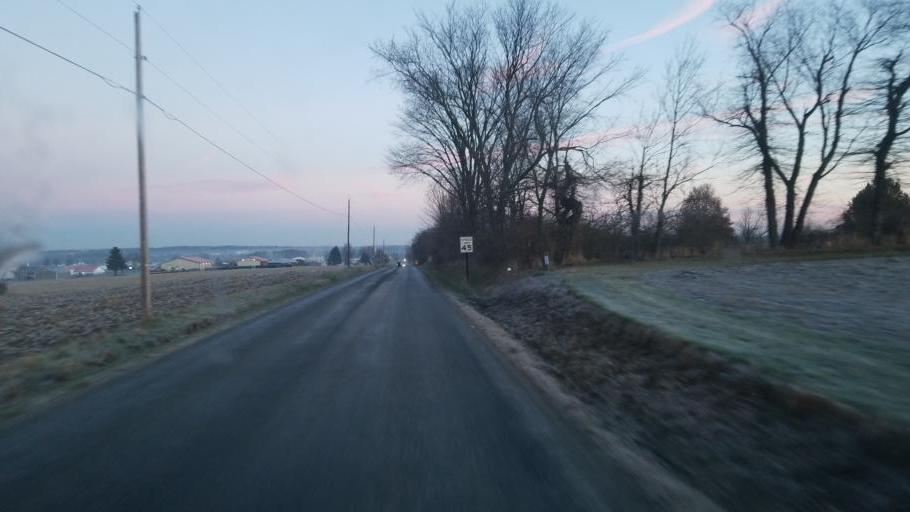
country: US
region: Ohio
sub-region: Wayne County
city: Orrville
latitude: 40.7890
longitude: -81.7752
